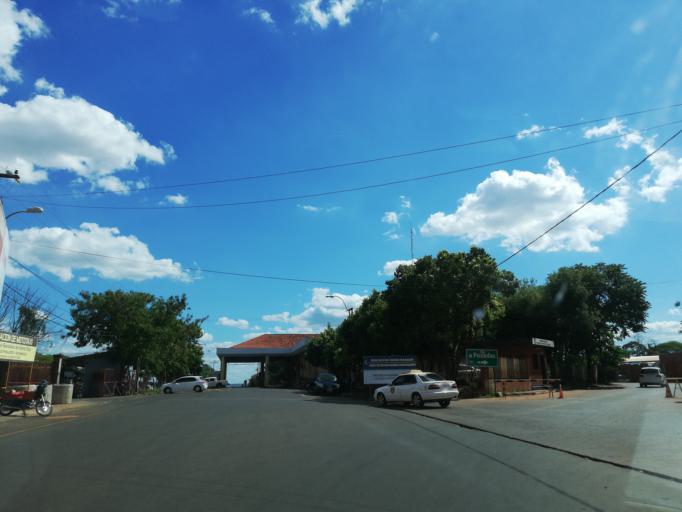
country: PY
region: Itapua
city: Encarnacion
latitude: -27.3625
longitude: -55.8526
